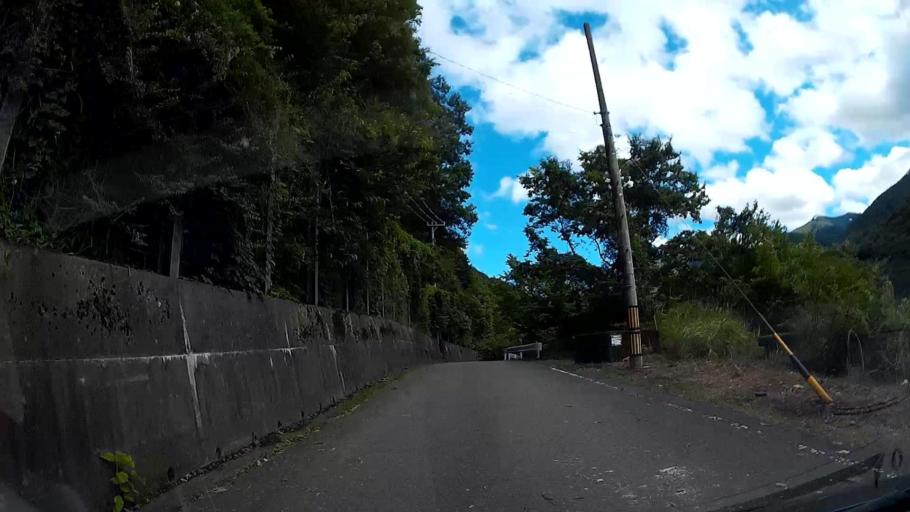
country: JP
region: Shizuoka
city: Shizuoka-shi
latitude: 35.3256
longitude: 138.1812
